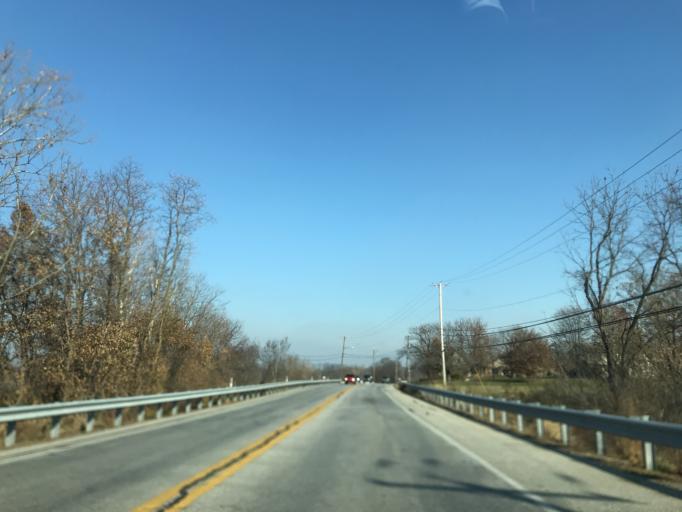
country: US
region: Pennsylvania
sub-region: York County
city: Pennville
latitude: 39.7588
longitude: -77.0332
